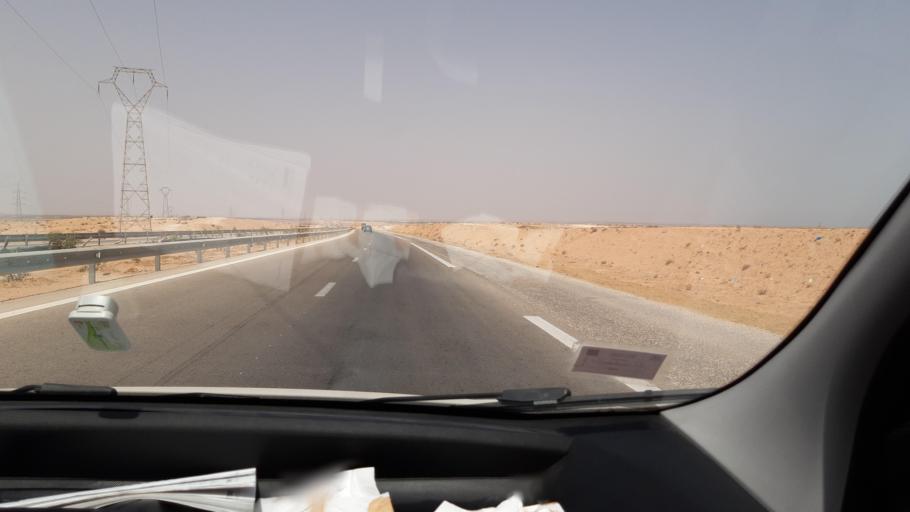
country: TN
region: Safaqis
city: Skhira
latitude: 34.1579
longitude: 9.9715
